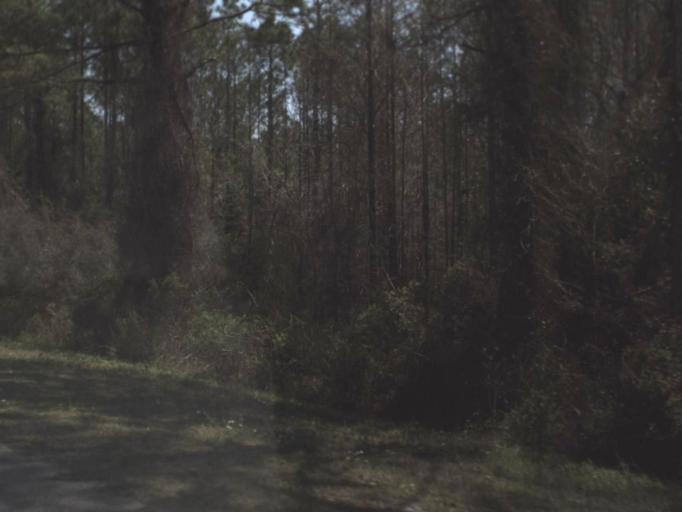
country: US
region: Florida
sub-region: Gulf County
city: Port Saint Joe
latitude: 29.7519
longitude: -85.2472
